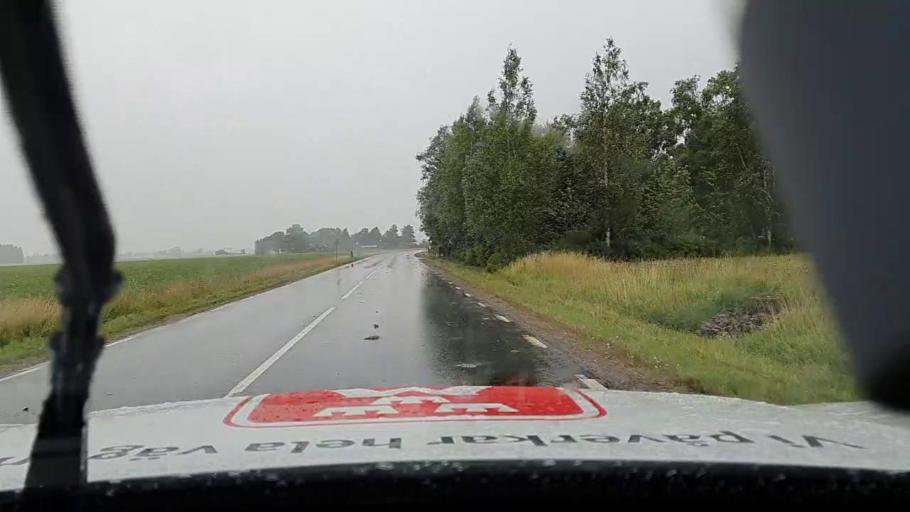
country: SE
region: Vaestra Goetaland
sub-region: Toreboda Kommun
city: Toereboda
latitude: 58.6595
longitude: 14.1274
